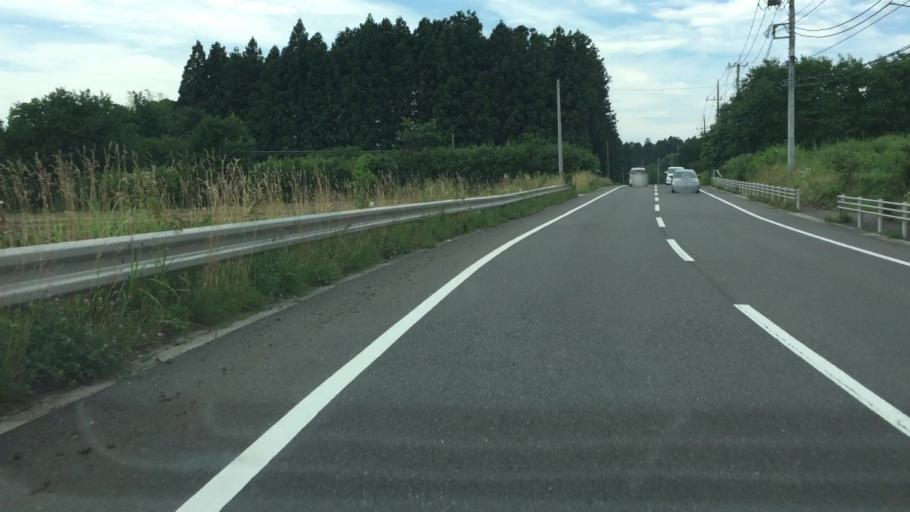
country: JP
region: Tochigi
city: Kuroiso
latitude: 37.0776
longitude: 140.0505
